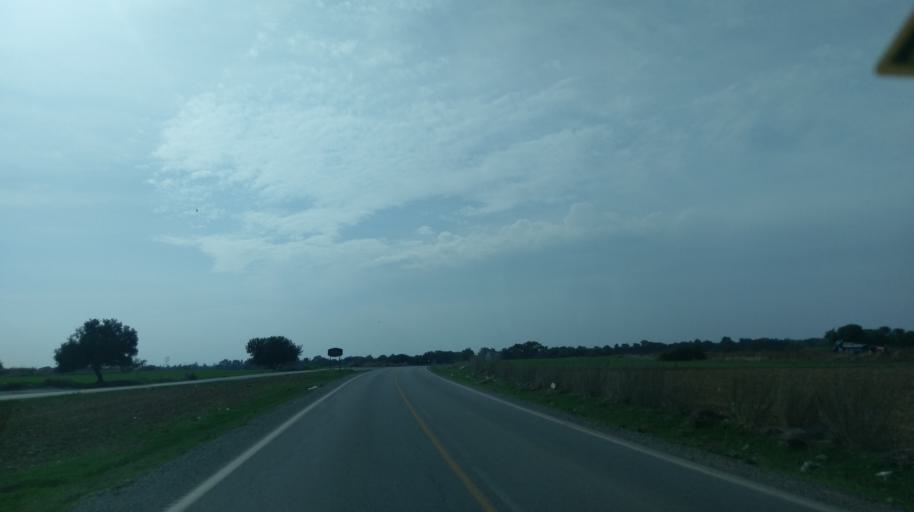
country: CY
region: Lefkosia
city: Morfou
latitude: 35.2973
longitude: 33.0446
